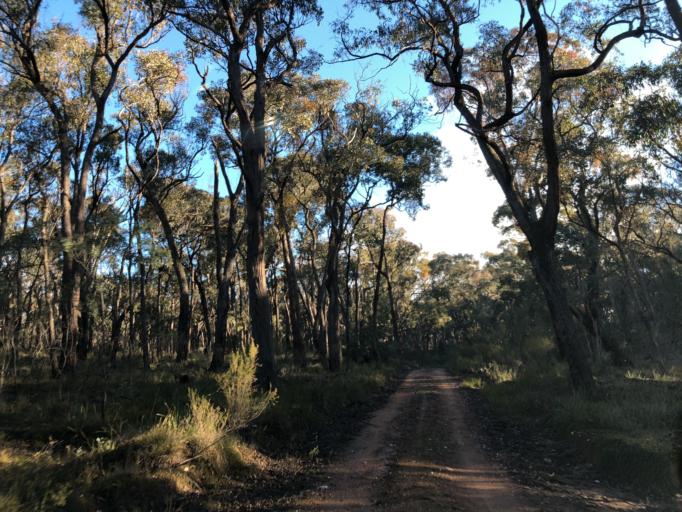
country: AU
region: Victoria
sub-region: Mount Alexander
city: Castlemaine
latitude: -37.2331
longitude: 144.2716
